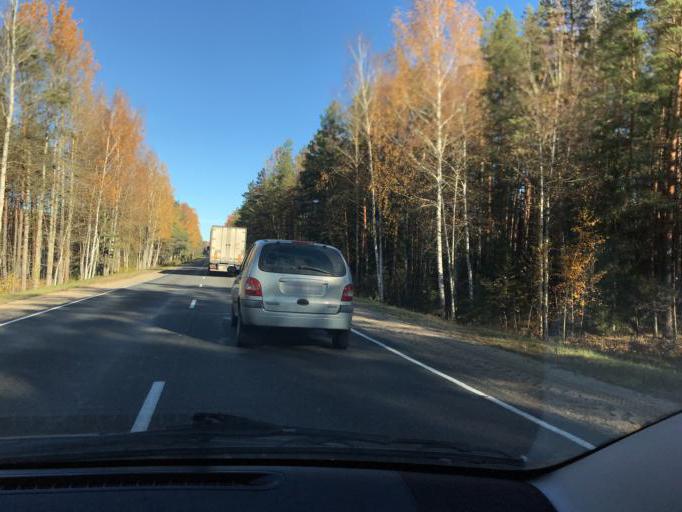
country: BY
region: Vitebsk
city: Polatsk
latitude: 55.3503
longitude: 28.8002
